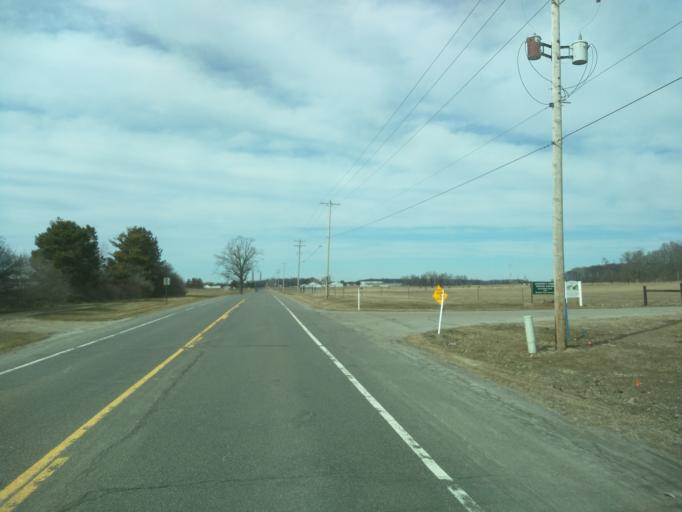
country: US
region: Michigan
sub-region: Ingham County
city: East Lansing
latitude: 42.6912
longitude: -84.4840
